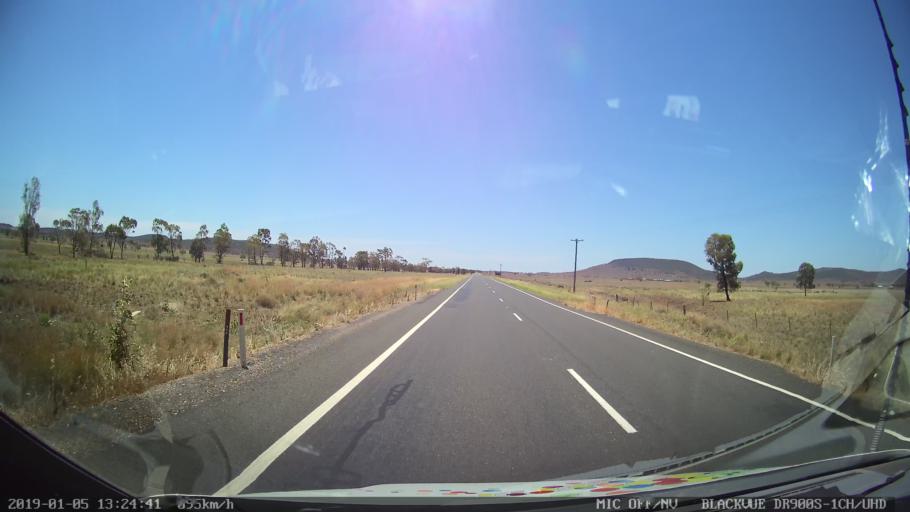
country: AU
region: New South Wales
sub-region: Gunnedah
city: Gunnedah
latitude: -31.0674
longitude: 149.9923
